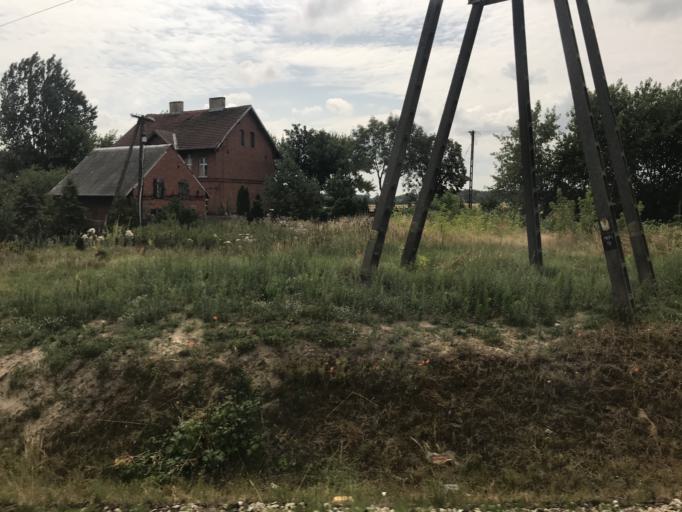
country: PL
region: Greater Poland Voivodeship
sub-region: Powiat gnieznienski
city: Trzemeszno
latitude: 52.5589
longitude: 17.7663
